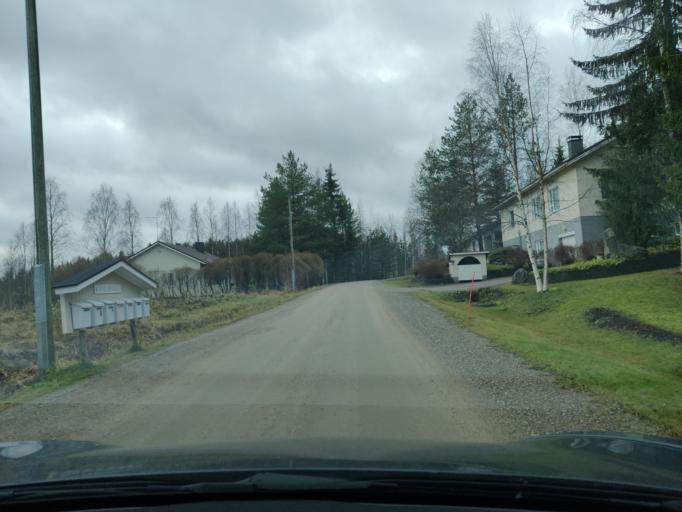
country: FI
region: Northern Savo
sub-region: Ylae-Savo
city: Kiuruvesi
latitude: 63.6403
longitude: 26.6412
